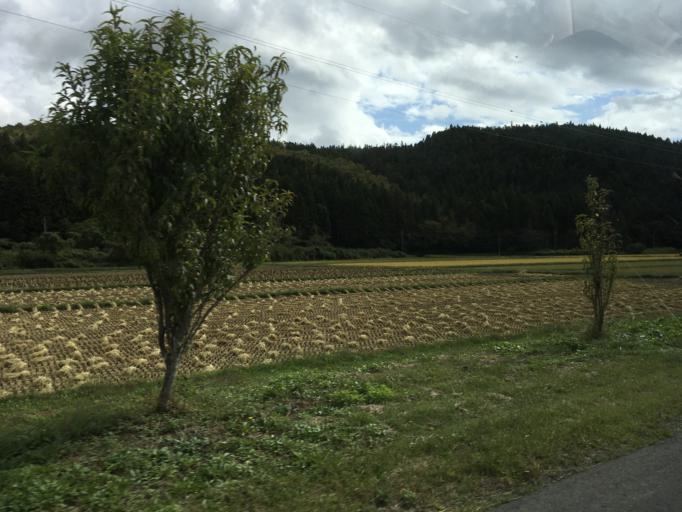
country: JP
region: Iwate
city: Ichinoseki
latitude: 38.7622
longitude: 141.3301
